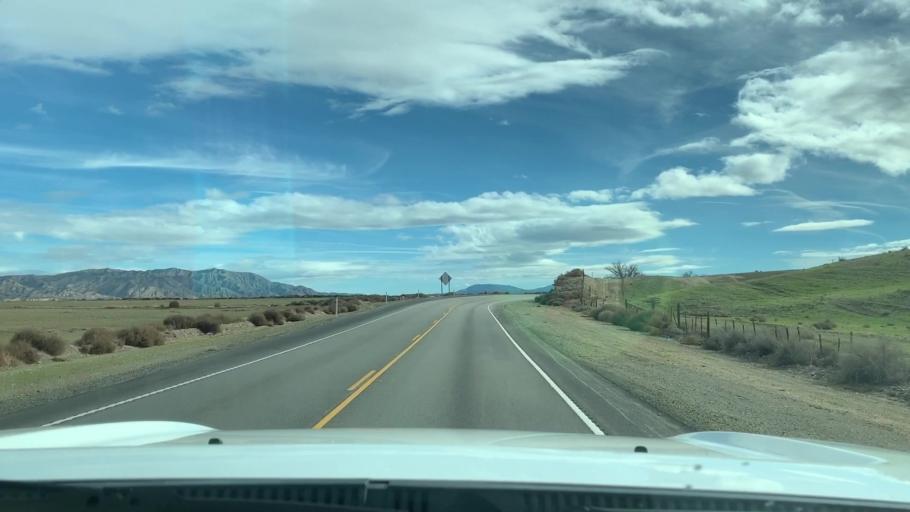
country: US
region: California
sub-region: Kern County
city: Taft Heights
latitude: 34.9640
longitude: -119.7245
